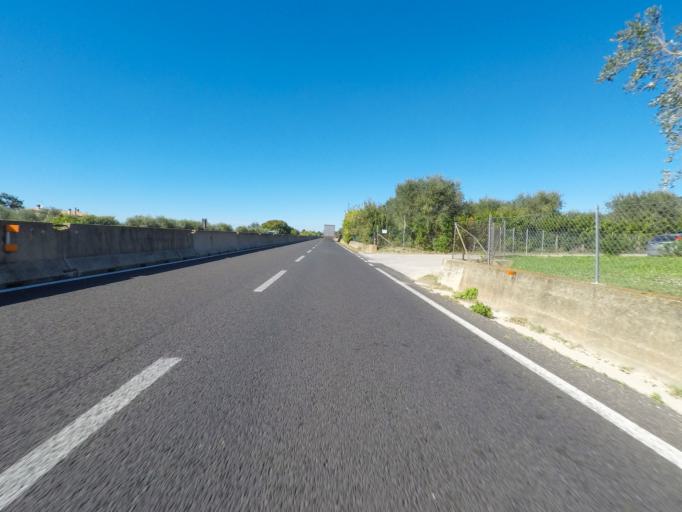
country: IT
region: Tuscany
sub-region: Provincia di Grosseto
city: Orbetello Scalo
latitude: 42.4601
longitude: 11.2463
